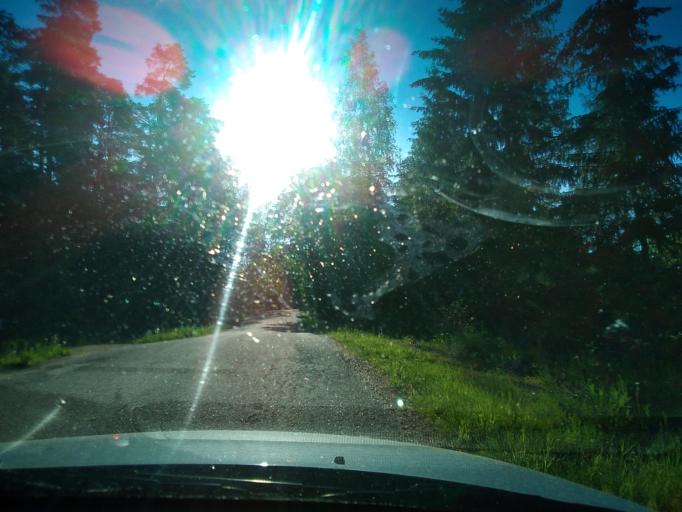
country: FI
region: Haeme
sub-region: Forssa
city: Tammela
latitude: 60.7736
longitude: 23.8139
